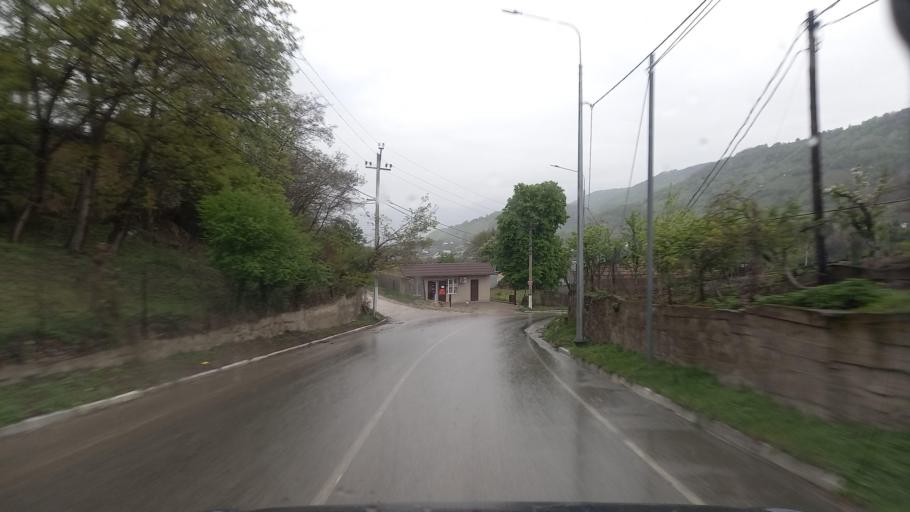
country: RU
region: Kabardino-Balkariya
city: Gundelen
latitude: 43.5993
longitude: 43.1582
